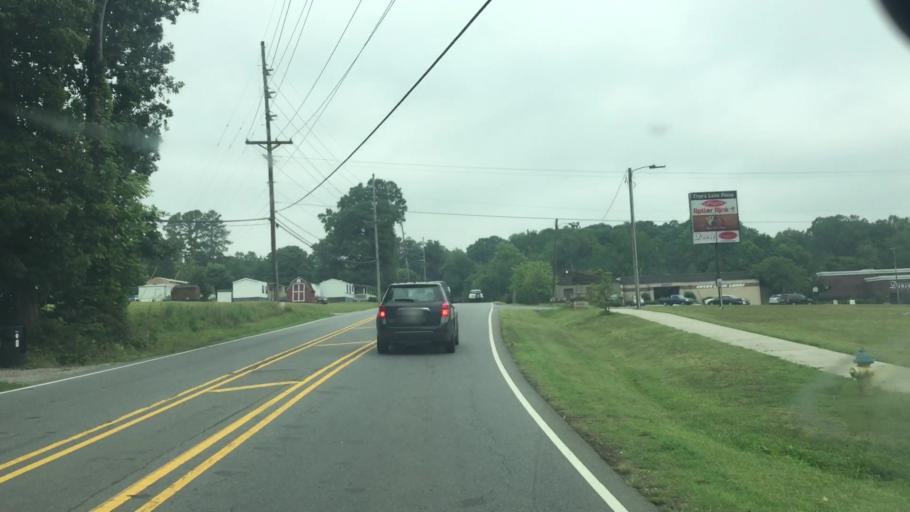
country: US
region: North Carolina
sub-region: Cabarrus County
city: Concord
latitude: 35.4119
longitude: -80.6239
